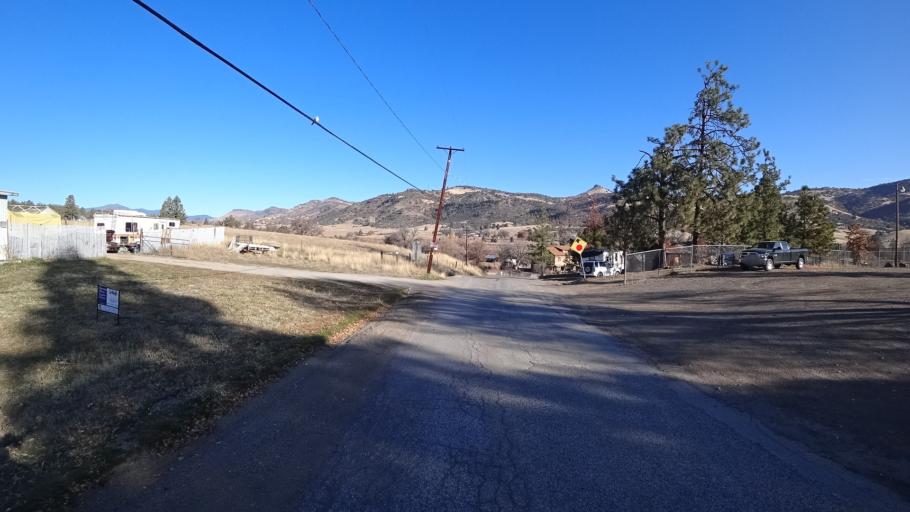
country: US
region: California
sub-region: Siskiyou County
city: Montague
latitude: 41.9115
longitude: -122.5618
